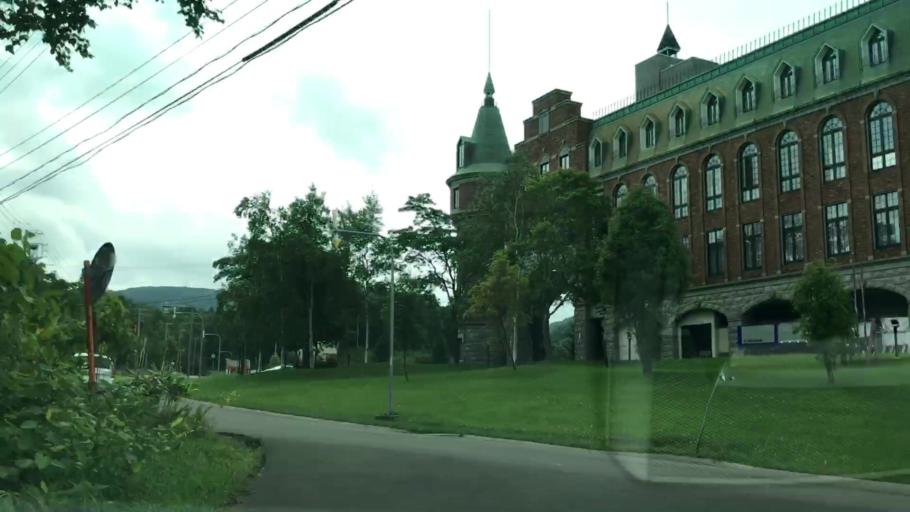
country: JP
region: Hokkaido
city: Yoichi
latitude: 43.1358
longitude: 140.8238
